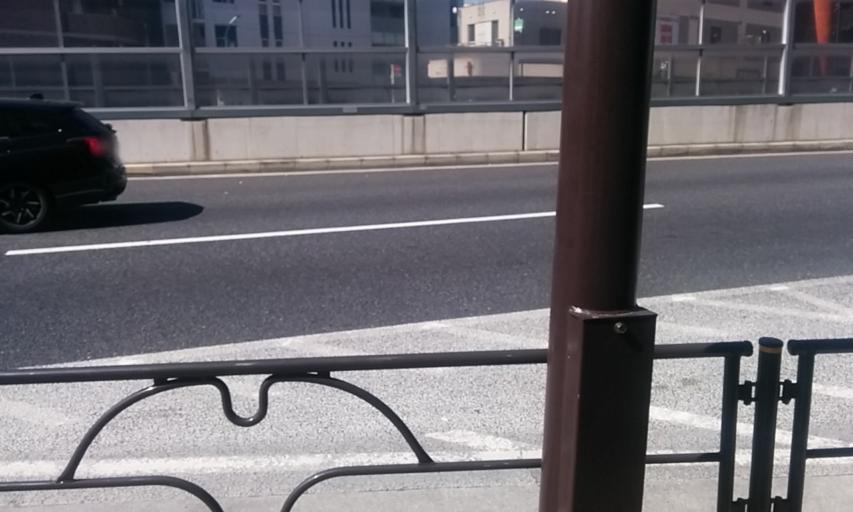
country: JP
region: Tokyo
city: Tokyo
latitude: 35.6741
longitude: 139.6879
